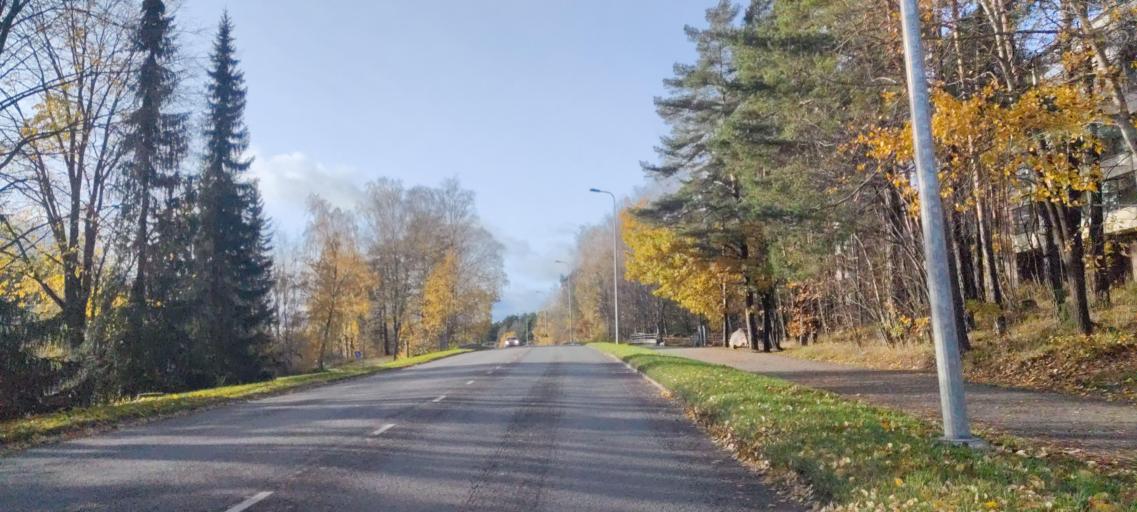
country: FI
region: Varsinais-Suomi
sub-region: Turku
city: Turku
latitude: 60.4772
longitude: 22.2488
